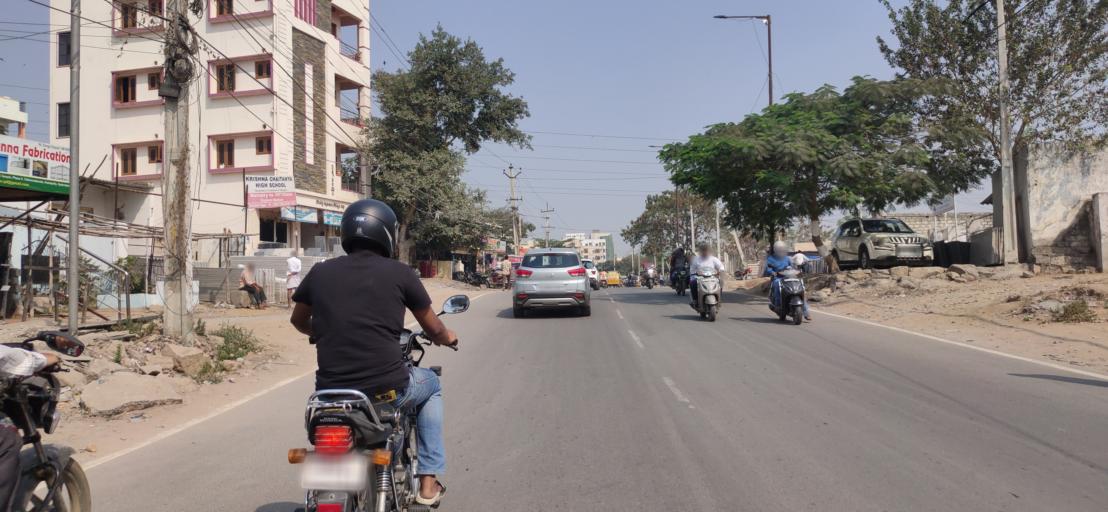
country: IN
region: Telangana
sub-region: Rangareddi
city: Kukatpalli
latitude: 17.5042
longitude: 78.4079
